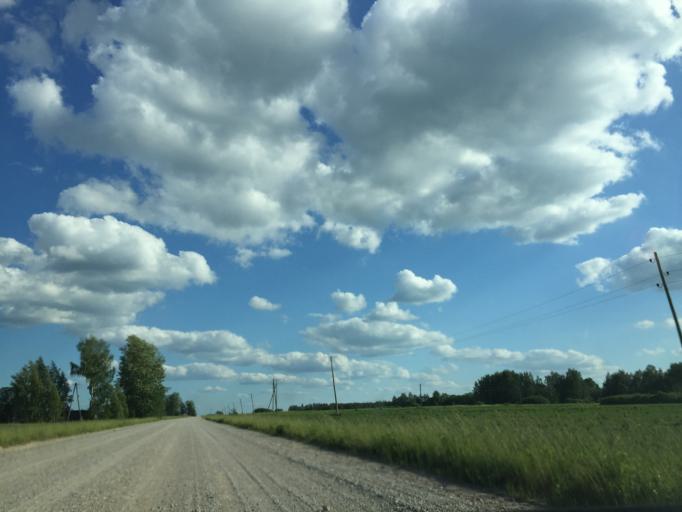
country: LV
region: Kandava
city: Kandava
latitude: 56.9148
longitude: 22.7910
